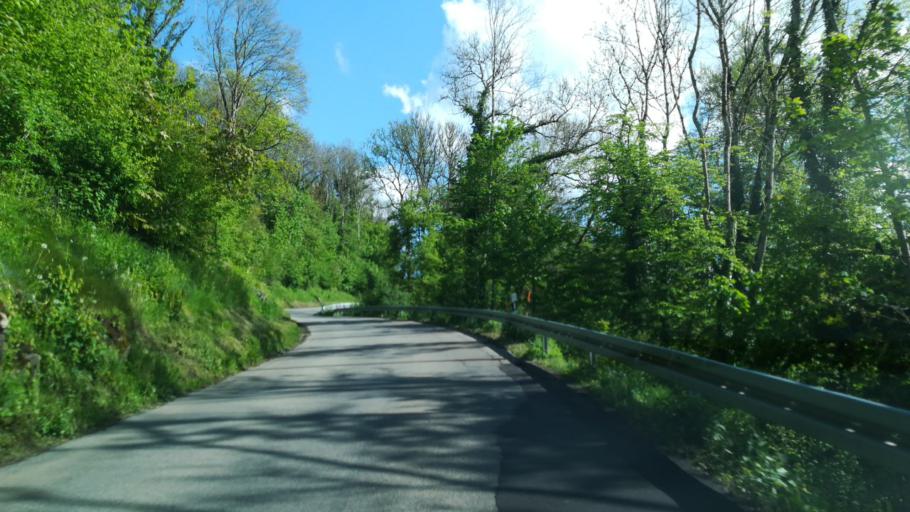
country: DE
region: Baden-Wuerttemberg
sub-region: Freiburg Region
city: Stuhlingen
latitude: 47.7418
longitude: 8.4365
